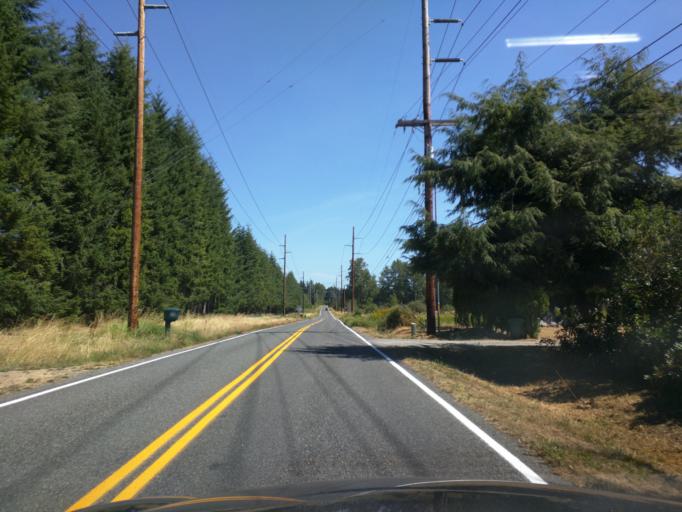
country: US
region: Washington
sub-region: Whatcom County
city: Geneva
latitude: 48.7936
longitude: -122.4287
